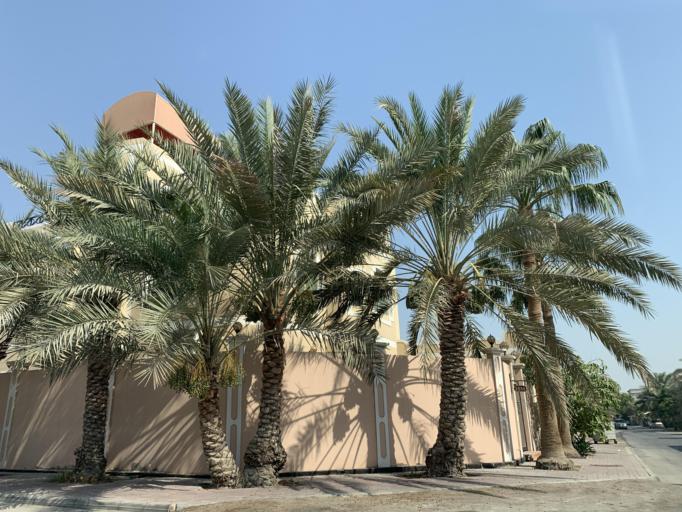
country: BH
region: Northern
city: Madinat `Isa
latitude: 26.1917
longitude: 50.5112
